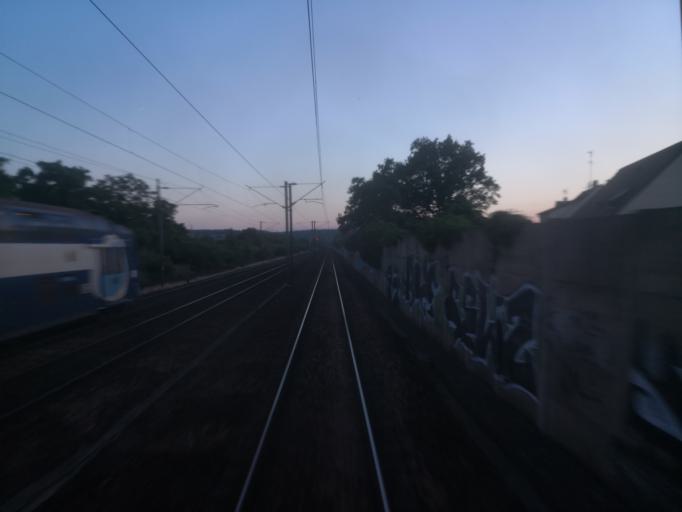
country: FR
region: Ile-de-France
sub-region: Departement des Yvelines
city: Aubergenville
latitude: 48.9701
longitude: 1.8418
